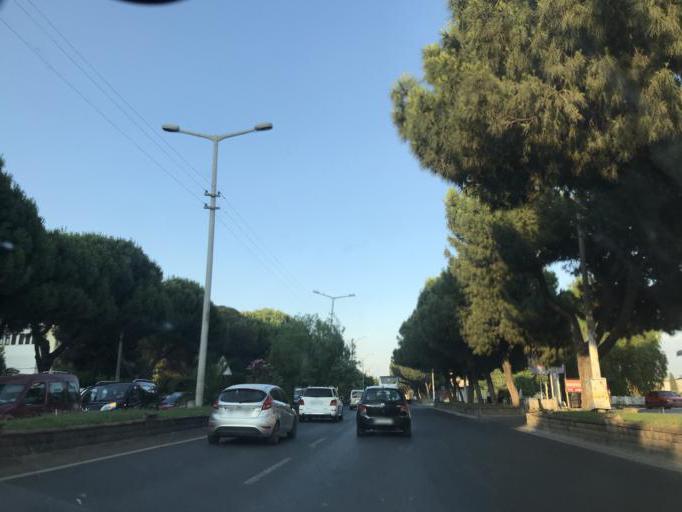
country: TR
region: Aydin
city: Nazilli
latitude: 37.9100
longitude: 28.3278
